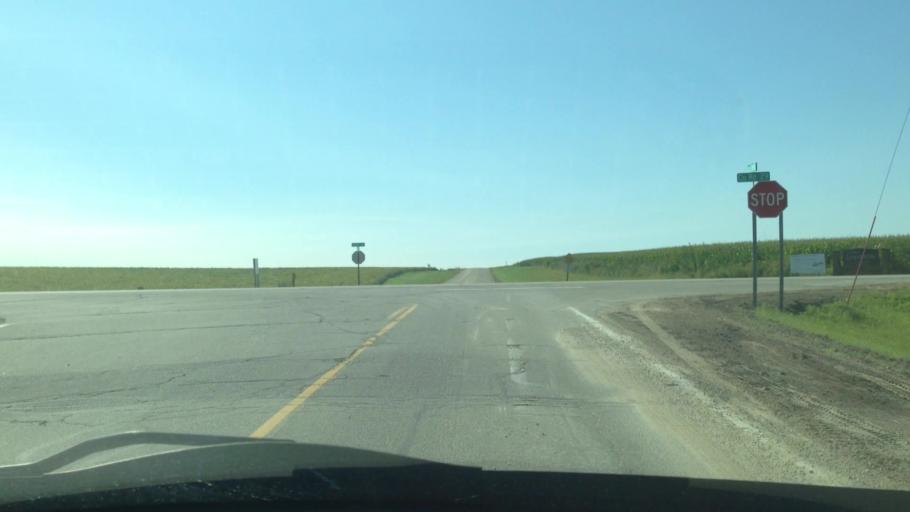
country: US
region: Minnesota
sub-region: Winona County
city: Lewiston
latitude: 43.9698
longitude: -91.8687
